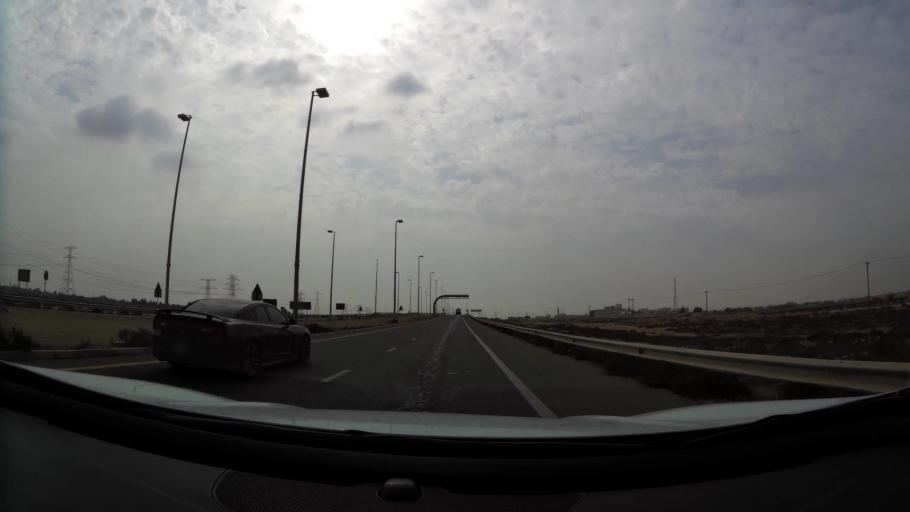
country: AE
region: Abu Dhabi
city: Abu Dhabi
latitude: 24.6641
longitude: 54.7416
